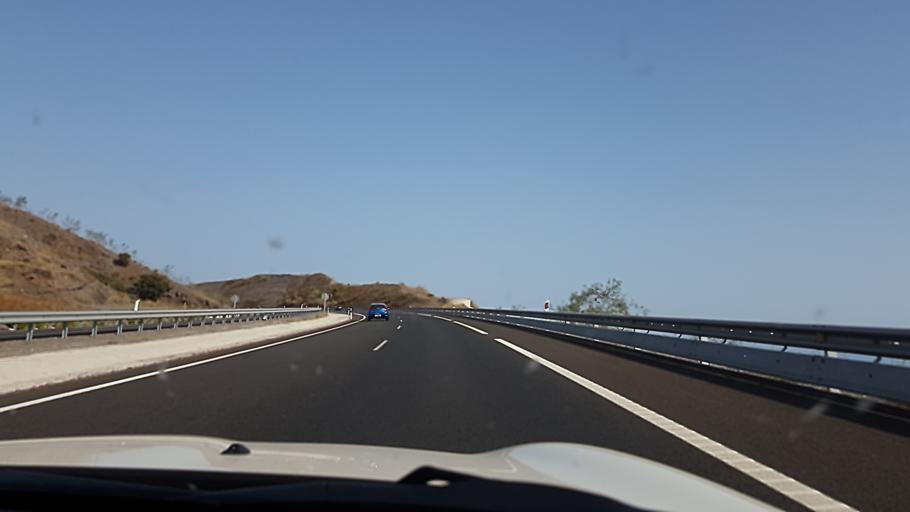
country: ES
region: Andalusia
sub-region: Provincia de Granada
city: Albunol
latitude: 36.7525
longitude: -3.2163
